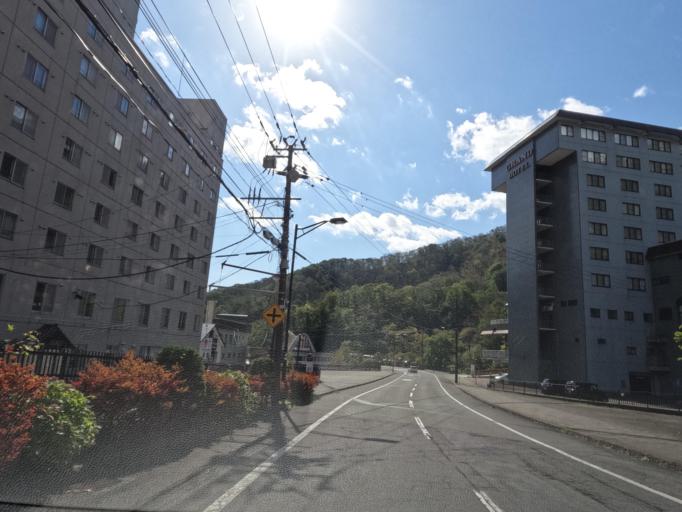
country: JP
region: Hokkaido
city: Shiraoi
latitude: 42.4926
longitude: 141.1426
